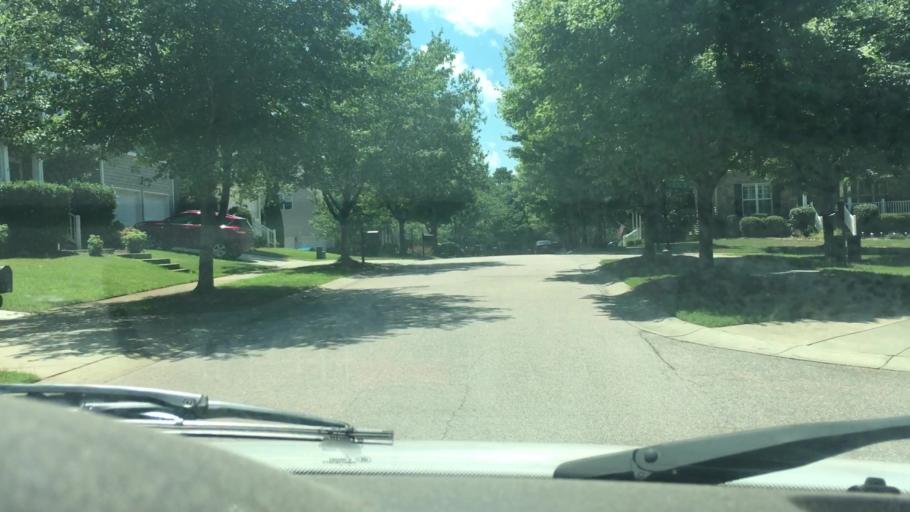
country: US
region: North Carolina
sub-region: Mecklenburg County
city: Cornelius
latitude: 35.4636
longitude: -80.8609
